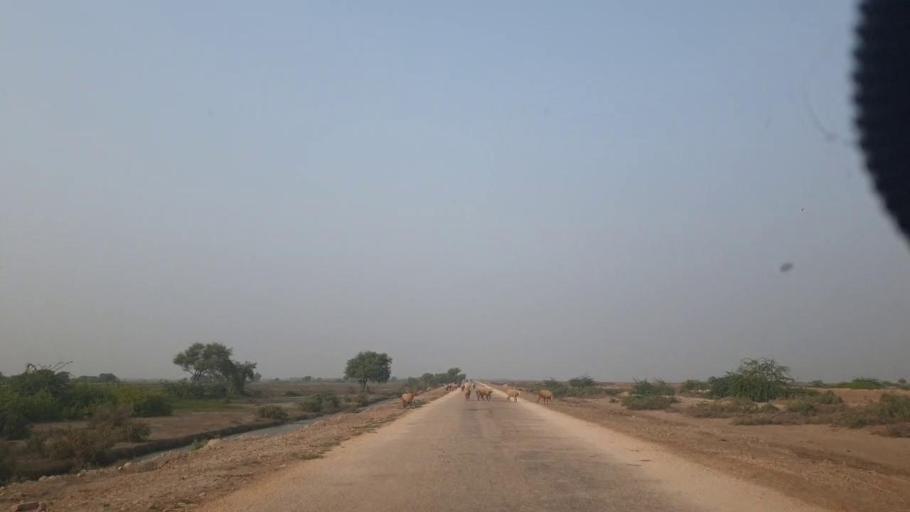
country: PK
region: Sindh
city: Bulri
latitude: 24.8421
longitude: 68.4039
